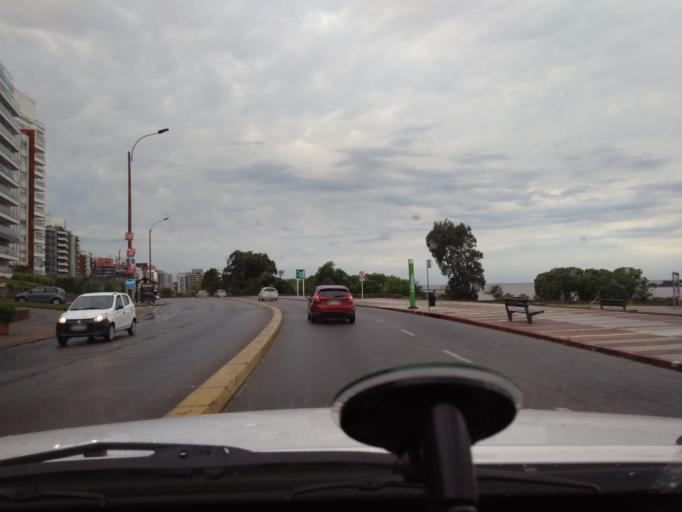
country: UY
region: Canelones
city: Paso de Carrasco
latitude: -34.8983
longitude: -56.1137
